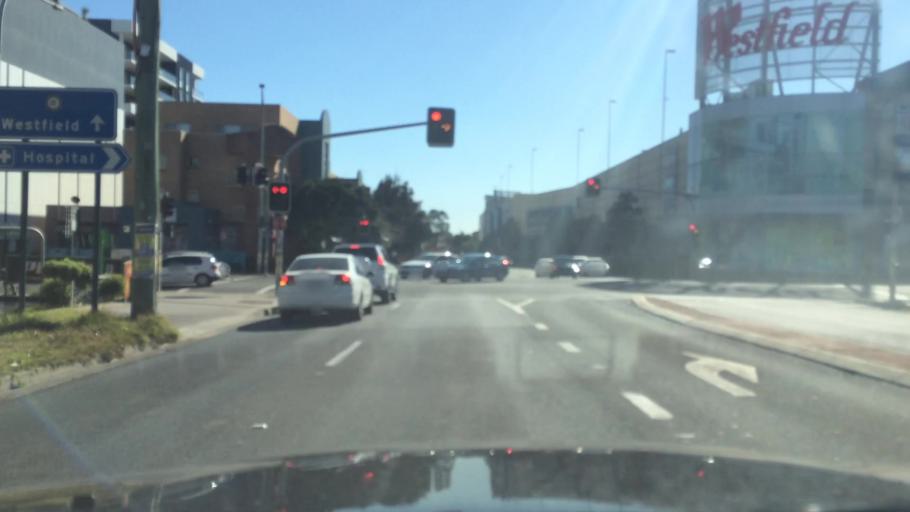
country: AU
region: New South Wales
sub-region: Fairfield
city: Liverpool
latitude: -33.9202
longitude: 150.9217
